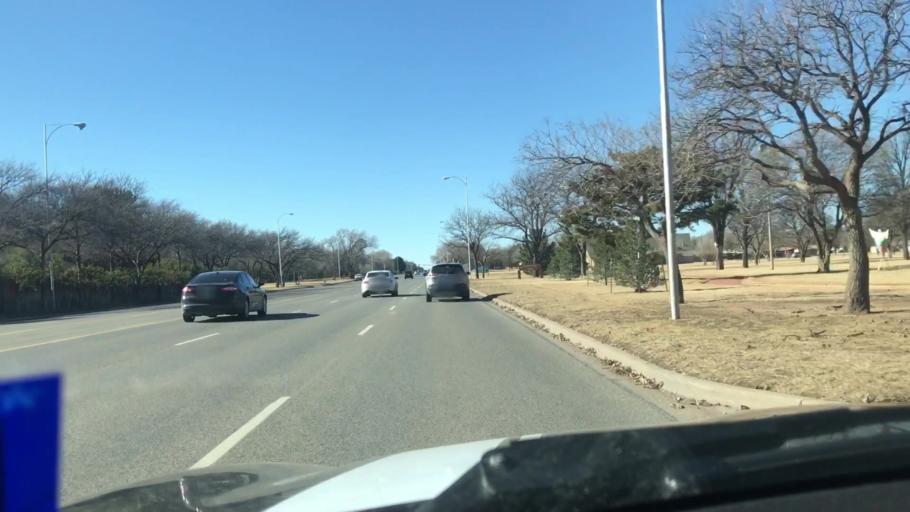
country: US
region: Texas
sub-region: Lubbock County
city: Lubbock
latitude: 33.5779
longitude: -101.9149
